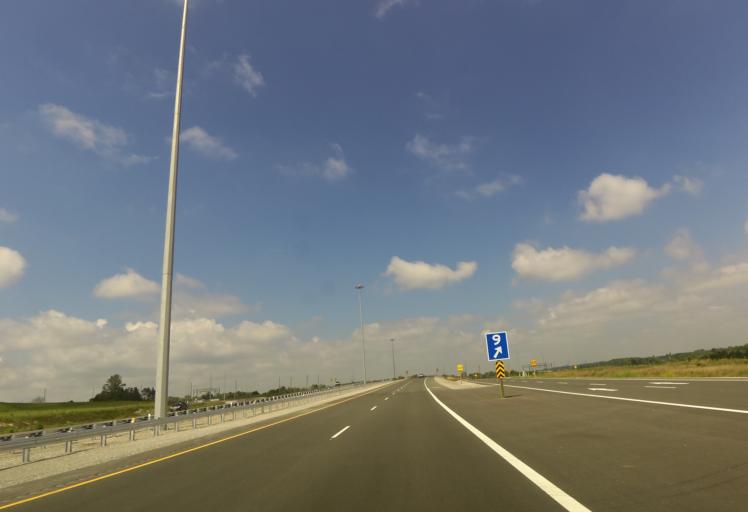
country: CA
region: Ontario
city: Ajax
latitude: 43.9384
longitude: -79.0051
